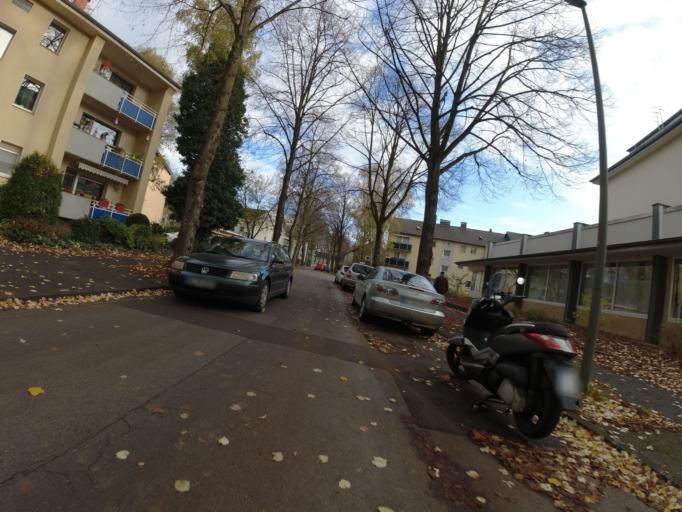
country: DE
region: North Rhine-Westphalia
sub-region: Regierungsbezirk Dusseldorf
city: Hochfeld
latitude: 51.4069
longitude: 6.6967
